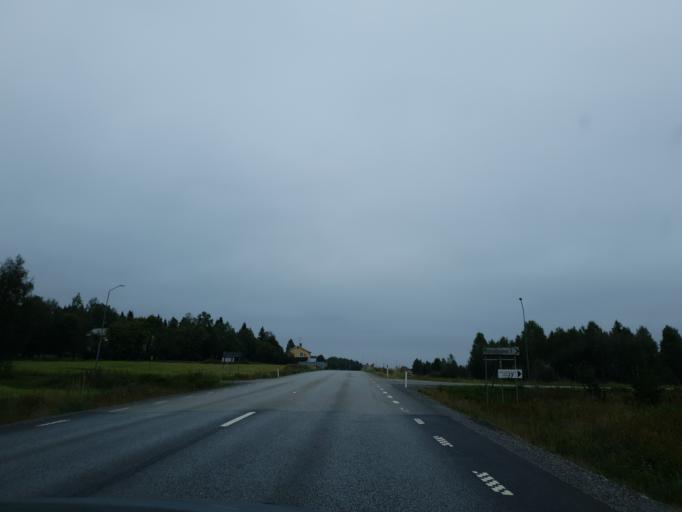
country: SE
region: Vaesterbotten
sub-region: Robertsfors Kommun
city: Robertsfors
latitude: 64.2284
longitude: 21.0163
